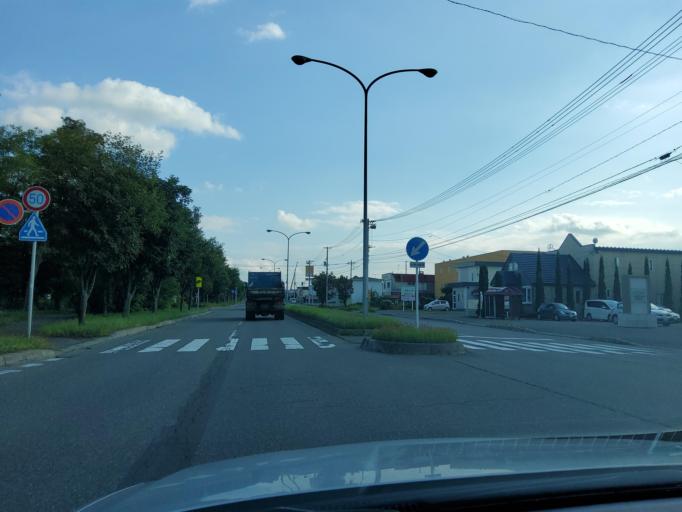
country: JP
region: Hokkaido
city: Obihiro
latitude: 42.9128
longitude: 143.2131
